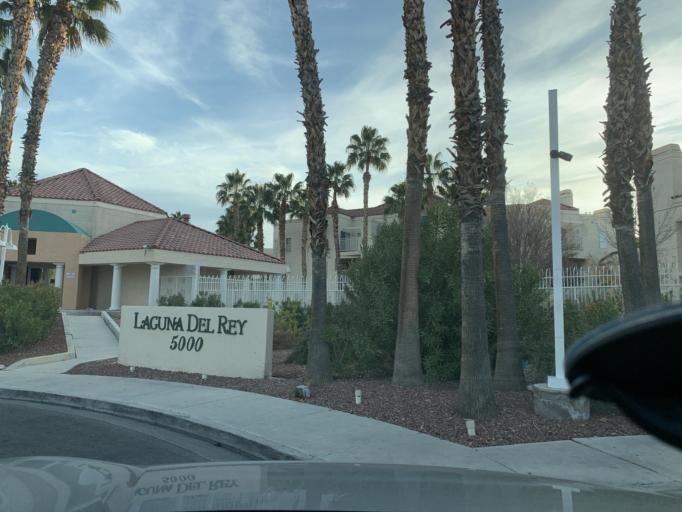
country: US
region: Nevada
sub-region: Clark County
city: Spring Valley
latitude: 36.0981
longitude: -115.2231
